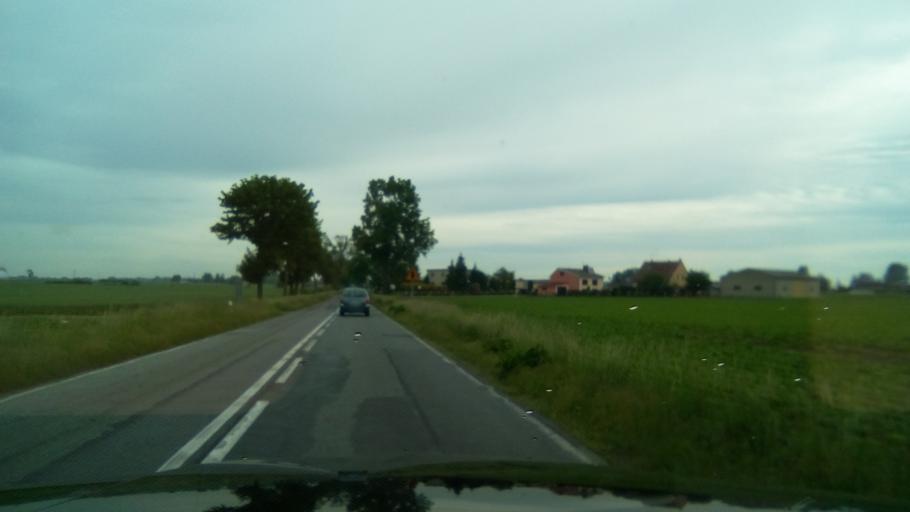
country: PL
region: Kujawsko-Pomorskie
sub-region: Powiat nakielski
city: Mrocza
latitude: 53.2112
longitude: 17.5904
